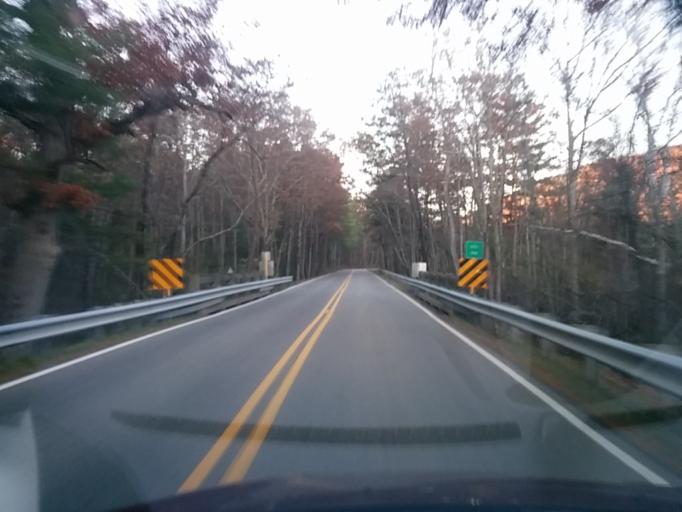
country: US
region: Virginia
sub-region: Rockbridge County
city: East Lexington
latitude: 37.9594
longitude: -79.4758
